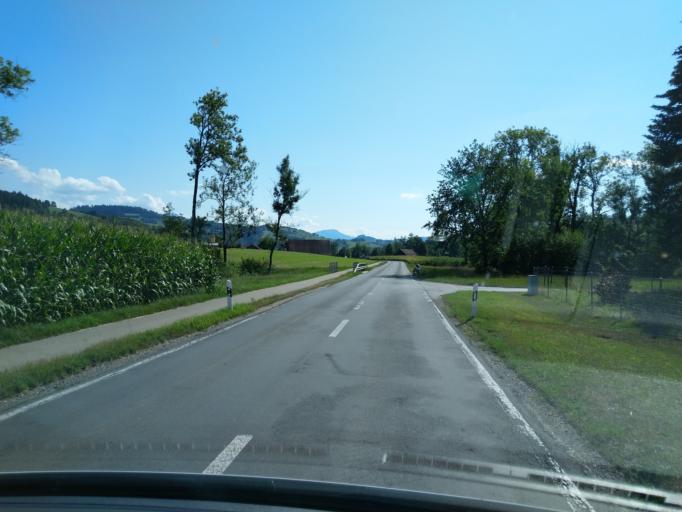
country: CH
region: Lucerne
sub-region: Sursee District
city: Ruswil
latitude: 47.0770
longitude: 8.1089
